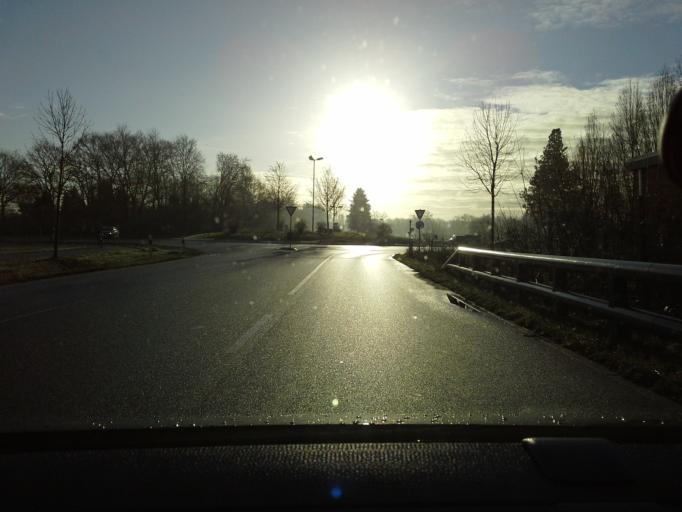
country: DE
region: Schleswig-Holstein
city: Pinneberg
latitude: 53.6451
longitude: 9.7701
